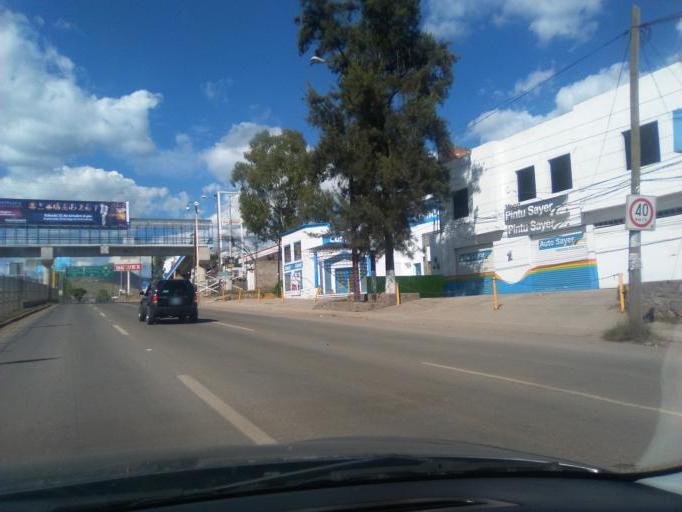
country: MX
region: Guanajuato
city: Marfil
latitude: 20.9890
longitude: -101.2851
